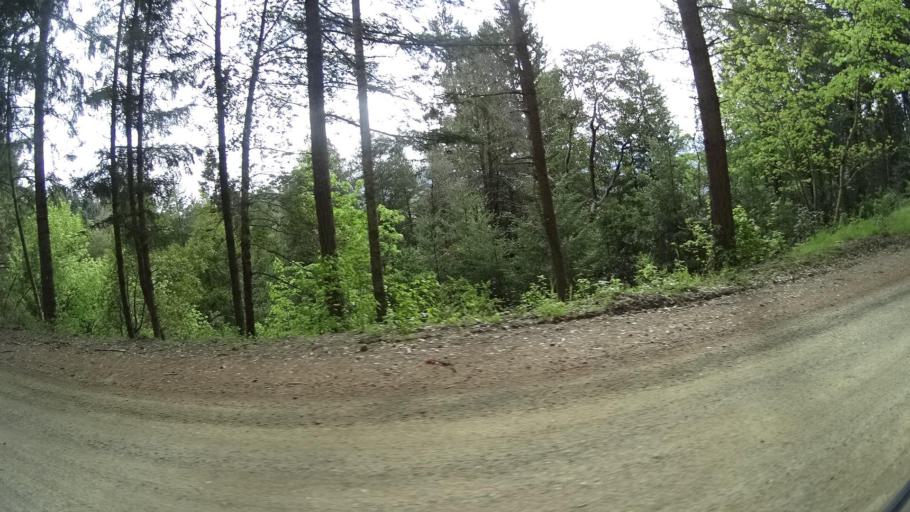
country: US
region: California
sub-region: Humboldt County
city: Redway
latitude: 40.2489
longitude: -123.7652
